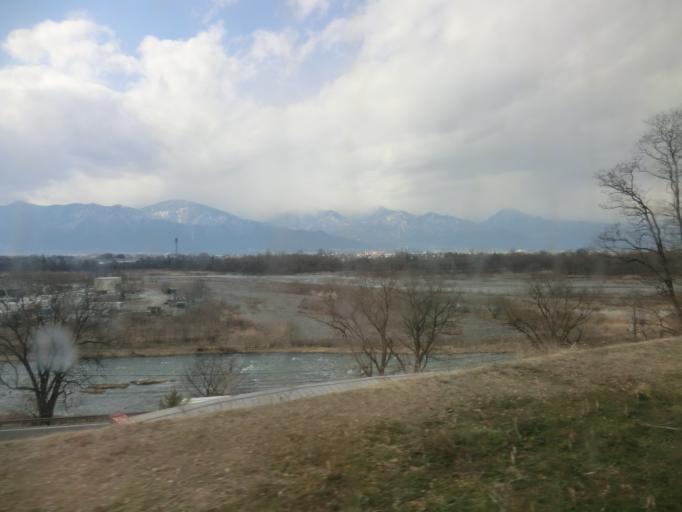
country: JP
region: Nagano
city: Matsumoto
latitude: 36.2753
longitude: 137.9479
